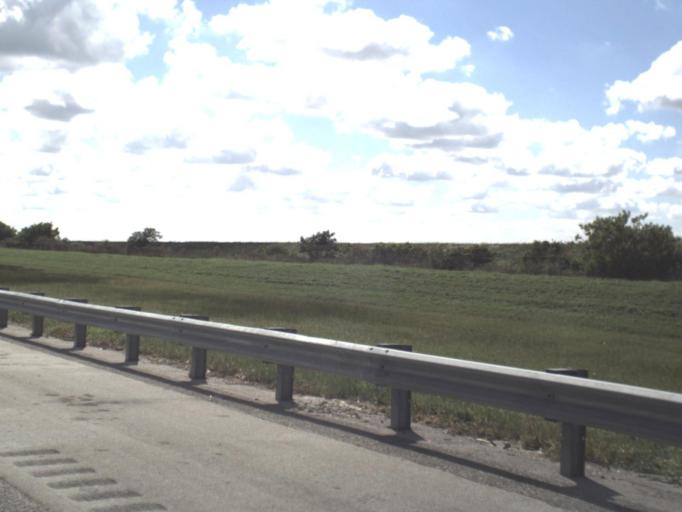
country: US
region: Florida
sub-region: Broward County
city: Coral Springs
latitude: 26.2400
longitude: -80.2973
